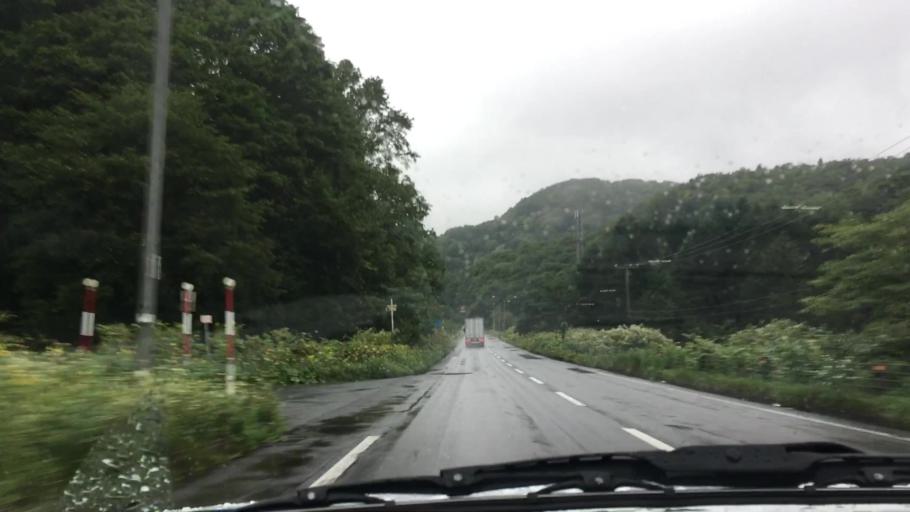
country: JP
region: Hokkaido
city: Niseko Town
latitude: 42.6016
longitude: 140.6209
